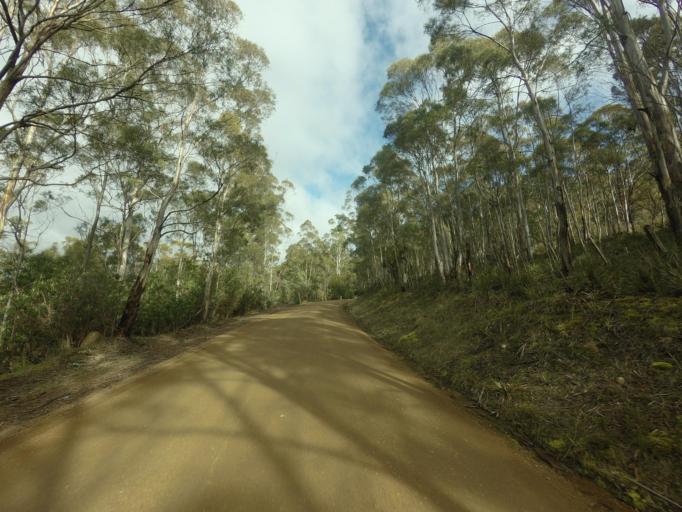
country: AU
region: Tasmania
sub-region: Derwent Valley
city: New Norfolk
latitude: -42.7869
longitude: 146.9376
